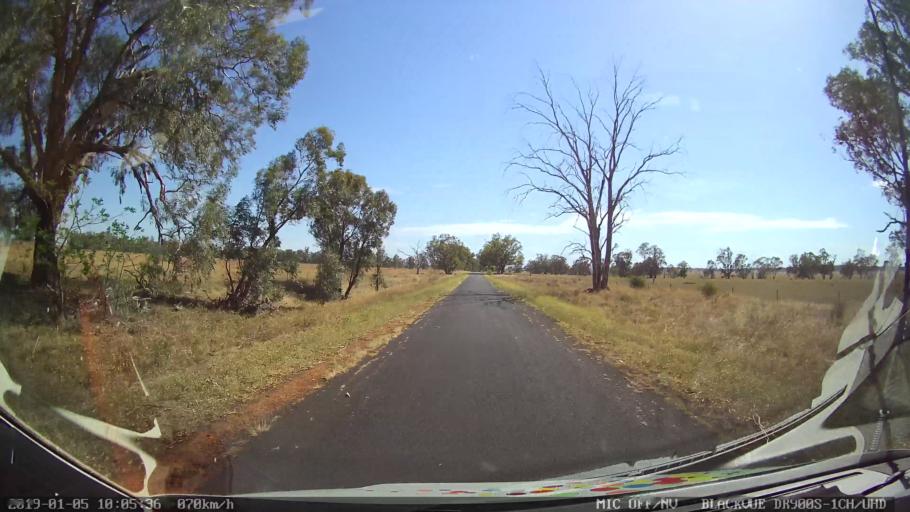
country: AU
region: New South Wales
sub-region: Gilgandra
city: Gilgandra
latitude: -31.6644
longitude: 148.8653
